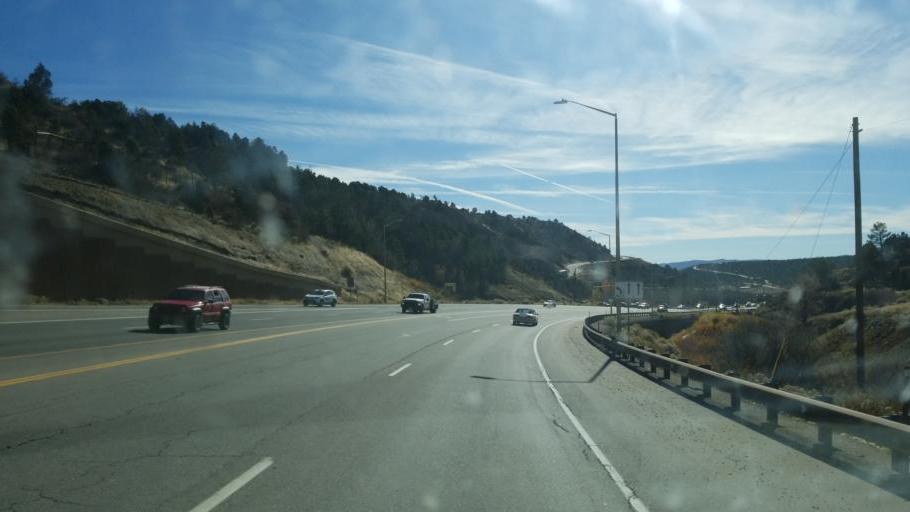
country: US
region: Colorado
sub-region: La Plata County
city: Durango
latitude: 37.2235
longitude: -107.8448
